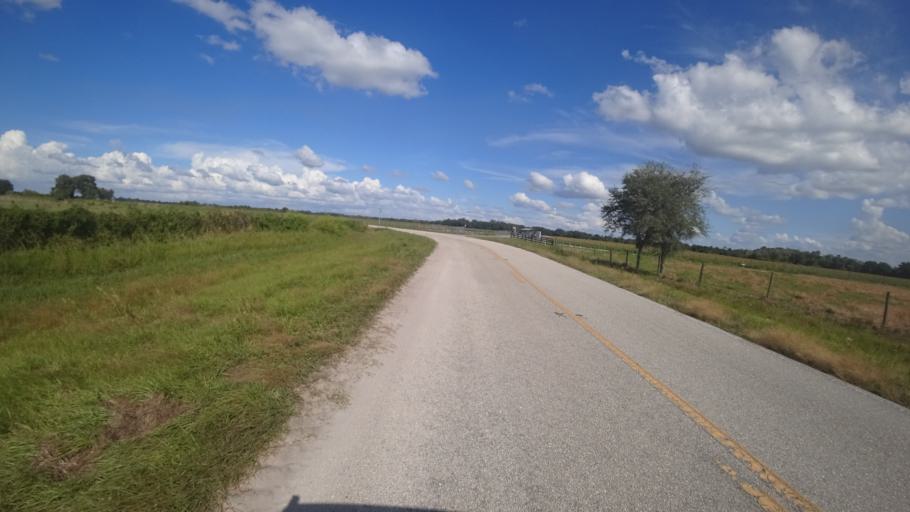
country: US
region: Florida
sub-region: DeSoto County
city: Arcadia
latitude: 27.2753
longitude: -82.0567
